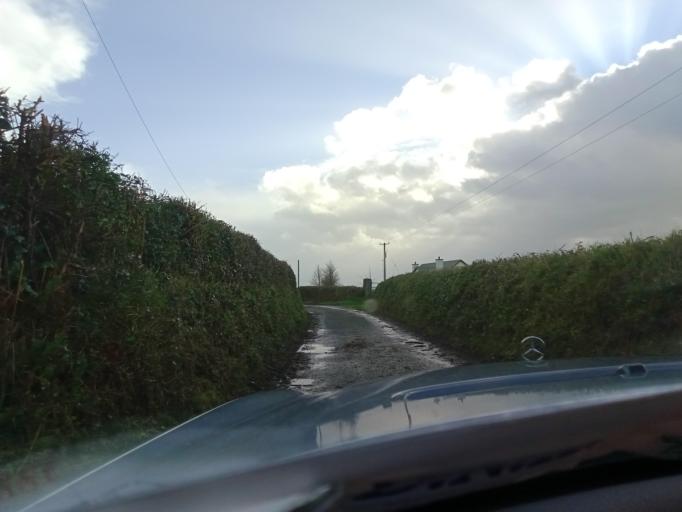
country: IE
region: Leinster
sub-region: Kilkenny
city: Mooncoin
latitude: 52.2877
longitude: -7.2719
